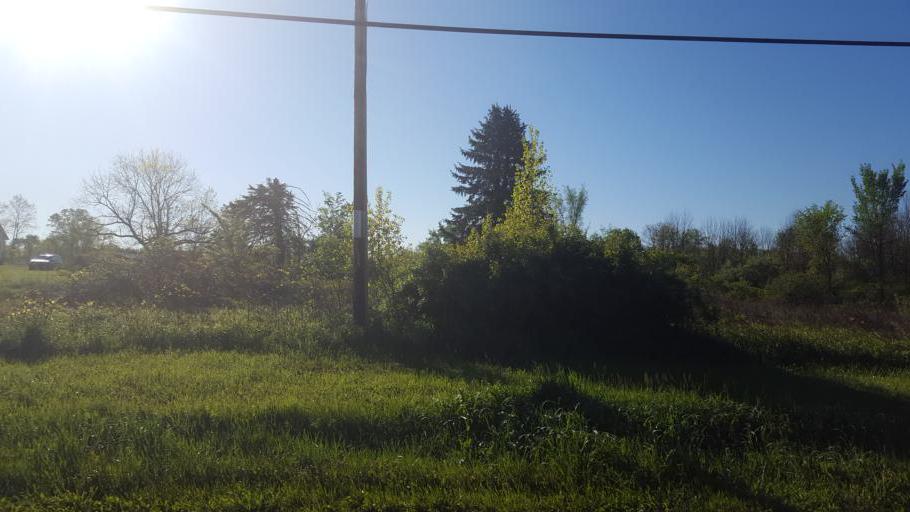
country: US
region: Ohio
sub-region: Delaware County
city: Sunbury
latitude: 40.3382
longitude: -82.8347
